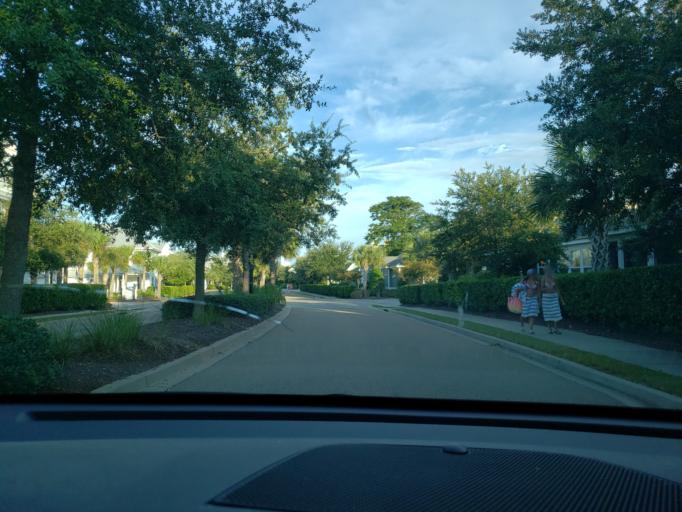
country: US
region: South Carolina
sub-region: Horry County
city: North Myrtle Beach
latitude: 33.7937
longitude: -78.7394
